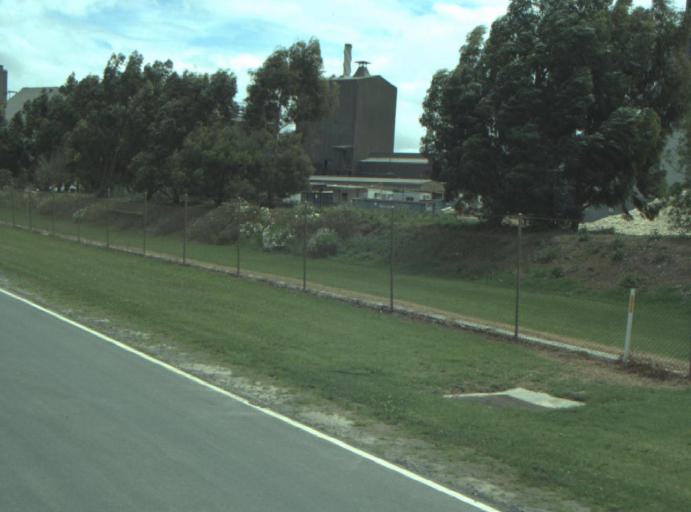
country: AU
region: Victoria
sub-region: Greater Geelong
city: Wandana Heights
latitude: -38.2263
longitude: 144.2701
